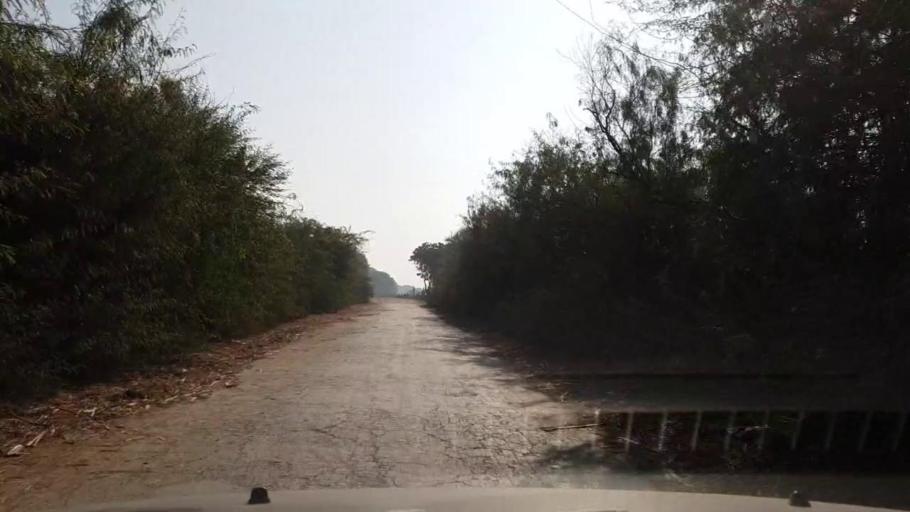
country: PK
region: Sindh
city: Matiari
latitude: 25.5481
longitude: 68.5461
